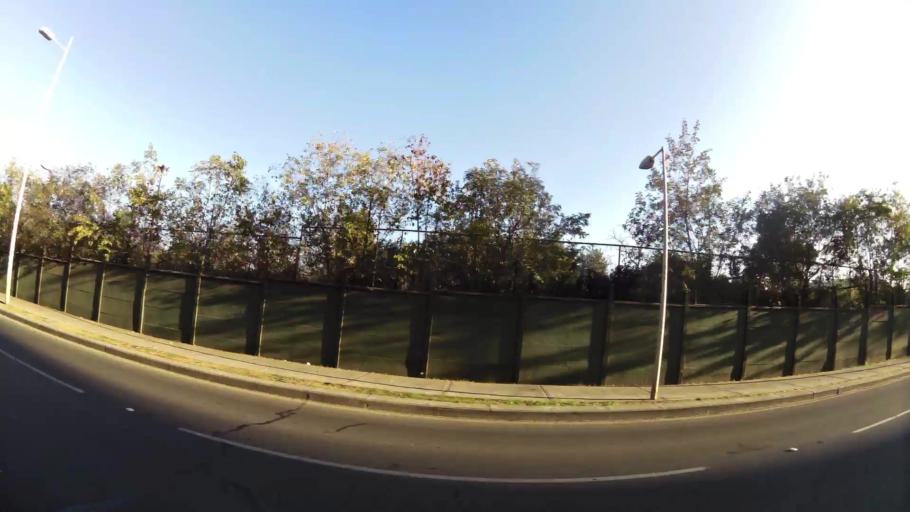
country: CL
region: Santiago Metropolitan
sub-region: Provincia de Santiago
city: Villa Presidente Frei, Nunoa, Santiago, Chile
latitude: -33.4114
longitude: -70.5897
